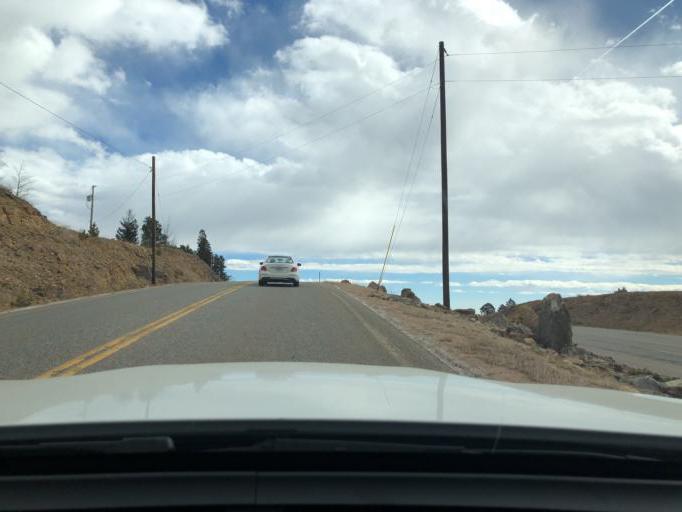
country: US
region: Colorado
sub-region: Gilpin County
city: Central City
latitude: 39.7903
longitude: -105.5137
